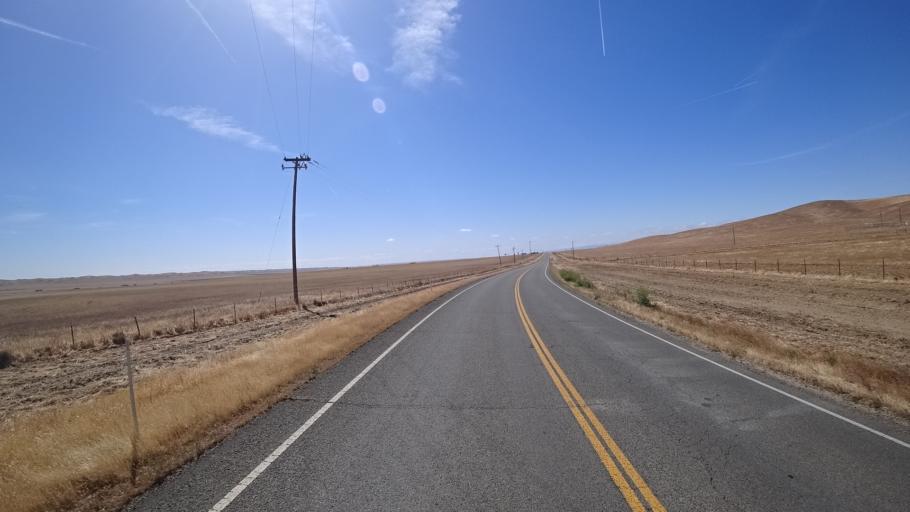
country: US
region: California
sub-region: Kings County
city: Avenal
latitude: 35.9022
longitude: -120.0535
